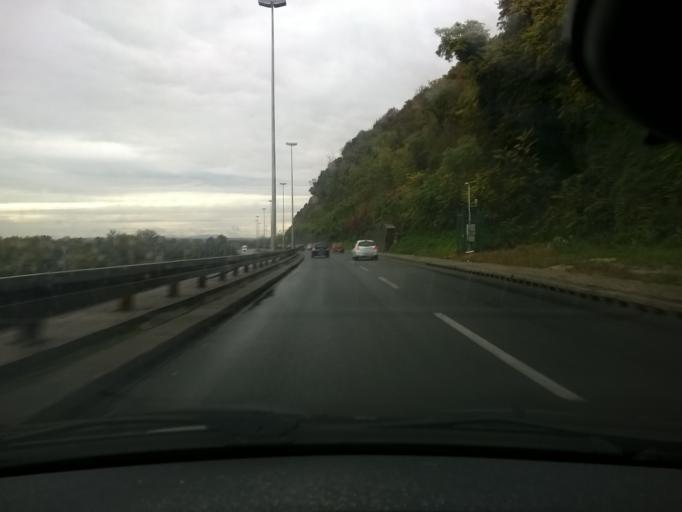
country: HR
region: Zagrebacka
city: Bestovje
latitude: 45.8273
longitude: 15.8259
